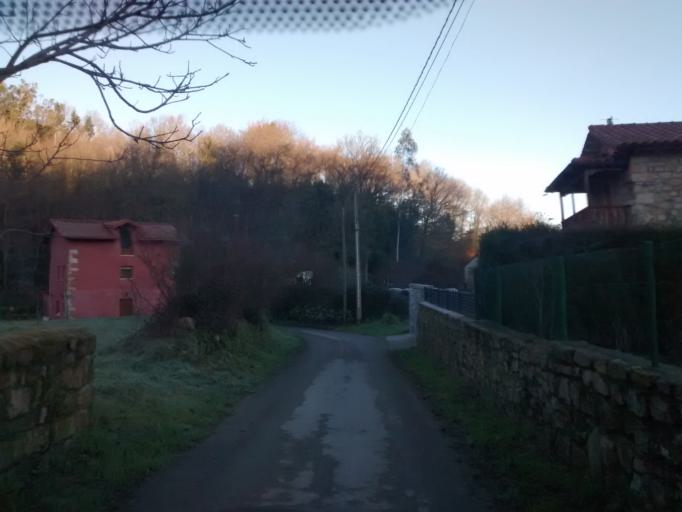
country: ES
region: Cantabria
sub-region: Provincia de Cantabria
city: Entrambasaguas
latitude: 43.3638
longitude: -3.7142
